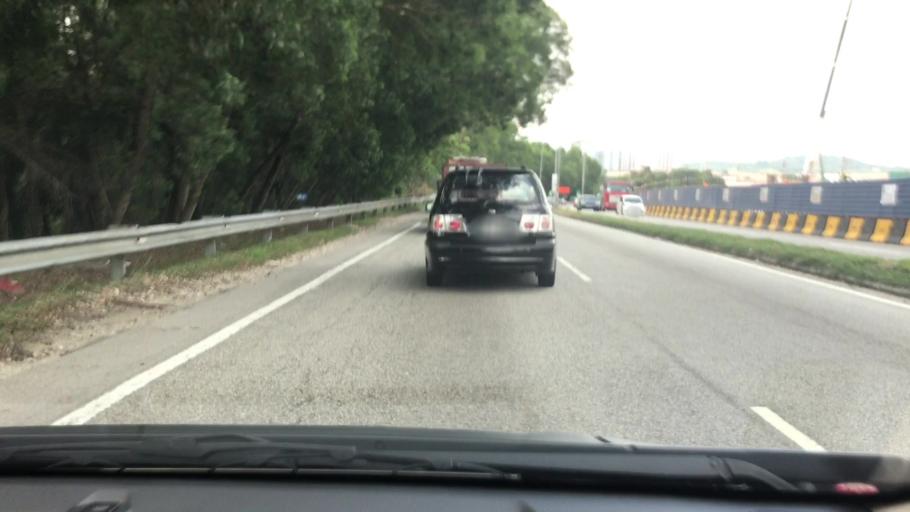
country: MY
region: Putrajaya
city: Putrajaya
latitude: 2.9838
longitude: 101.6612
